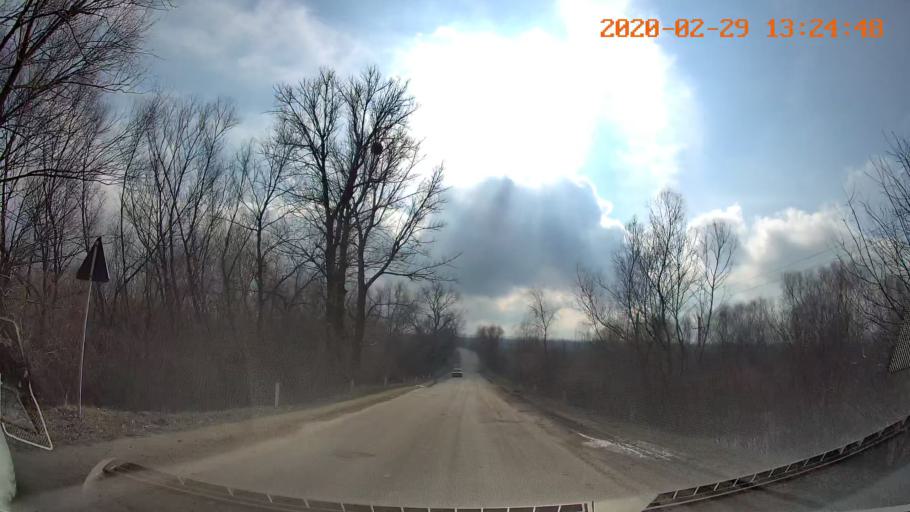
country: MD
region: Telenesti
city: Camenca
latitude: 47.9352
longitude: 28.6286
